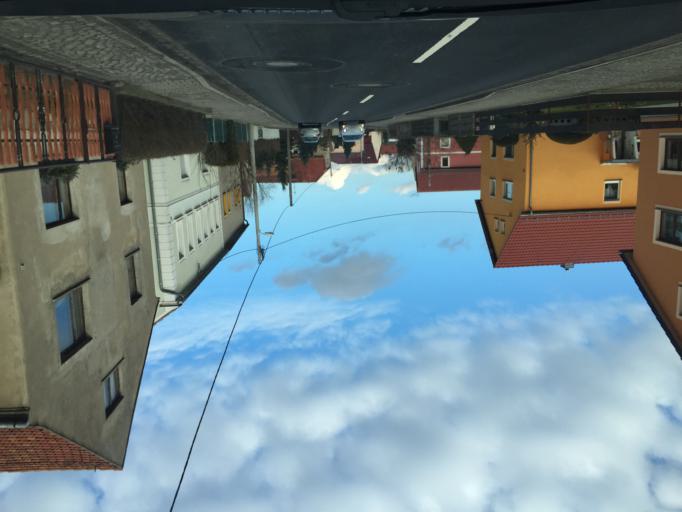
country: DE
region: Saxony
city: Radeburg
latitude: 51.1997
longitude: 13.7727
